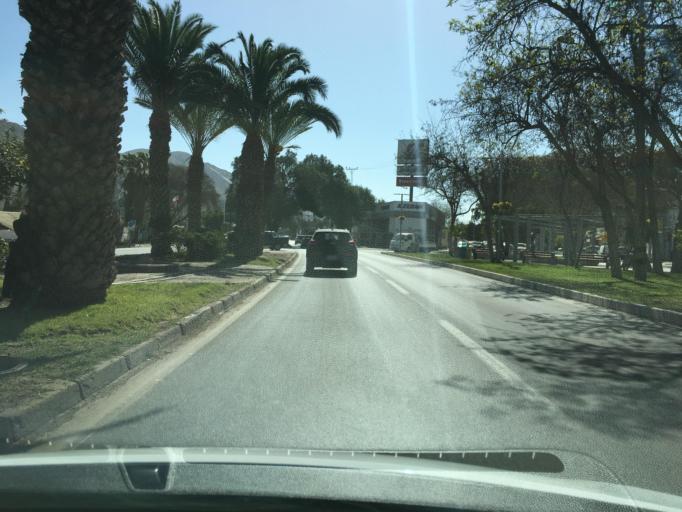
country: CL
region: Atacama
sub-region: Provincia de Copiapo
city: Copiapo
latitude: -27.3725
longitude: -70.3301
